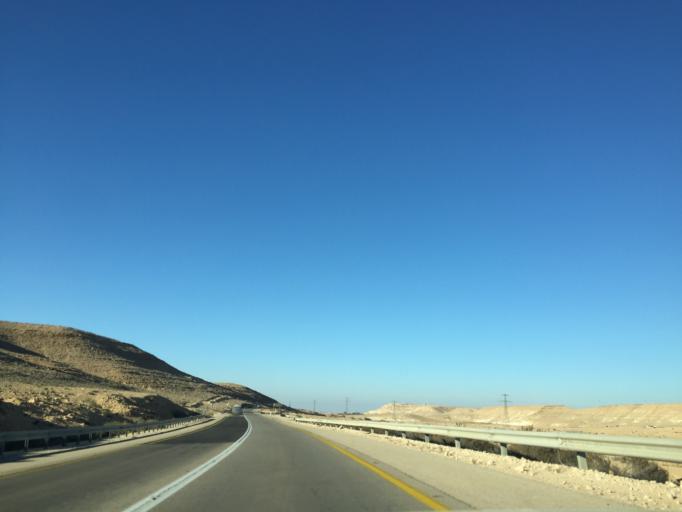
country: IL
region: Southern District
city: Midreshet Ben-Gurion
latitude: 30.7599
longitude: 34.7731
